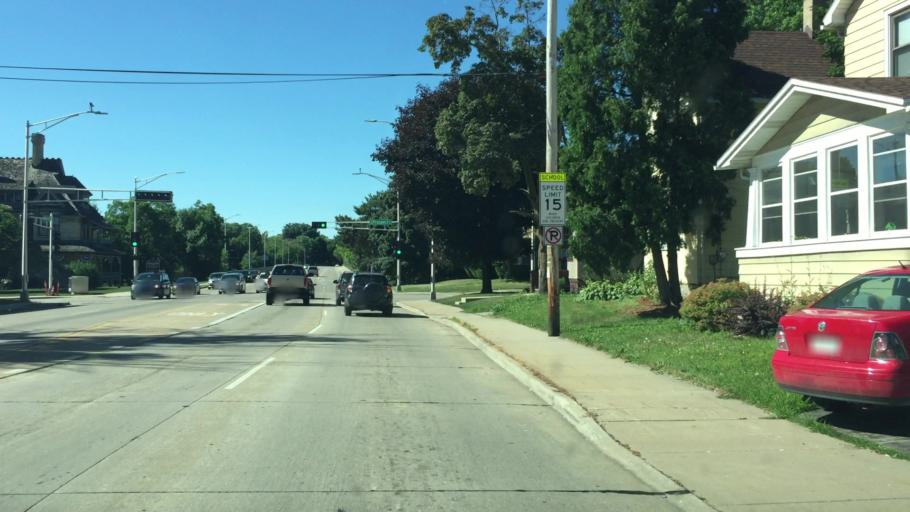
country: US
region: Wisconsin
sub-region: Outagamie County
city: Appleton
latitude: 44.2552
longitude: -88.4155
